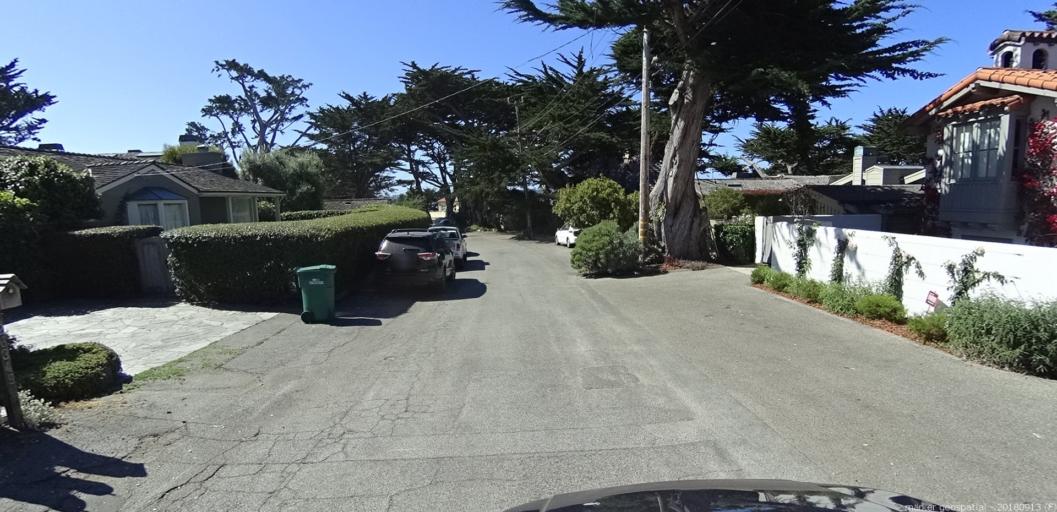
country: US
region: California
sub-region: Monterey County
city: Carmel-by-the-Sea
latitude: 36.5412
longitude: -121.9316
